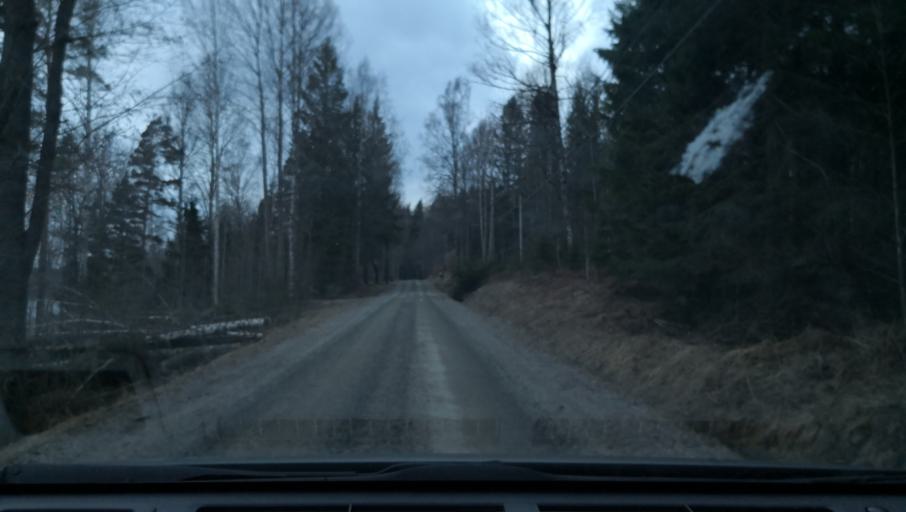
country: SE
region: Vaestmanland
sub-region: Kopings Kommun
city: Kolsva
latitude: 59.5945
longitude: 15.7181
